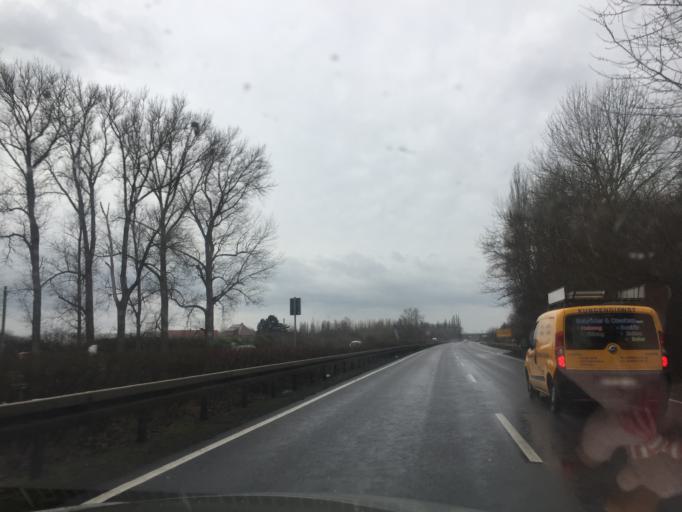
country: DE
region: Saxony-Anhalt
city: Diesdorf
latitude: 52.0768
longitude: 11.5761
